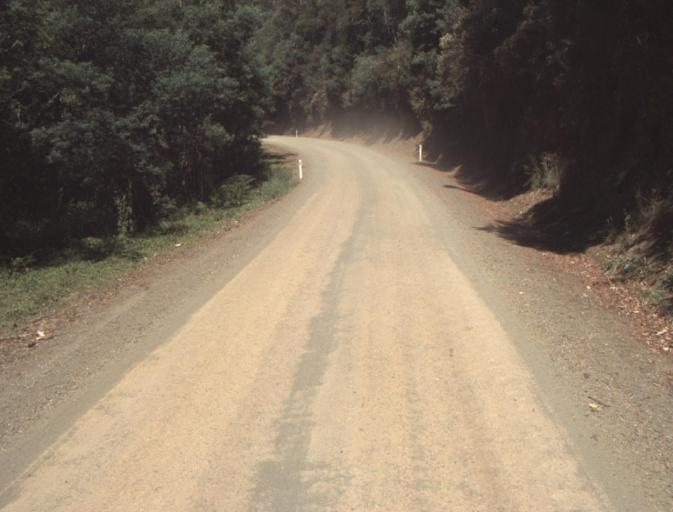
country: AU
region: Tasmania
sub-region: Dorset
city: Scottsdale
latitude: -41.3181
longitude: 147.4077
